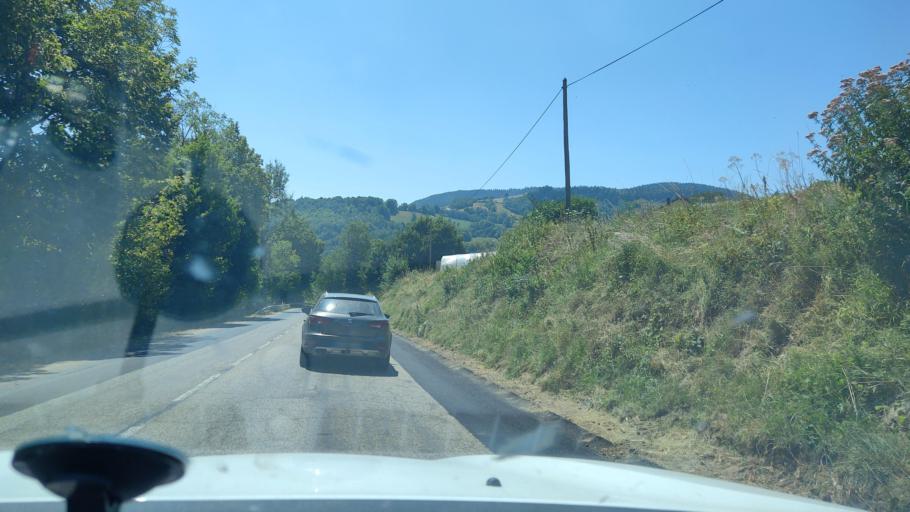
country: FR
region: Rhone-Alpes
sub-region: Departement de la Savoie
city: Barby
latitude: 45.6271
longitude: 6.0074
